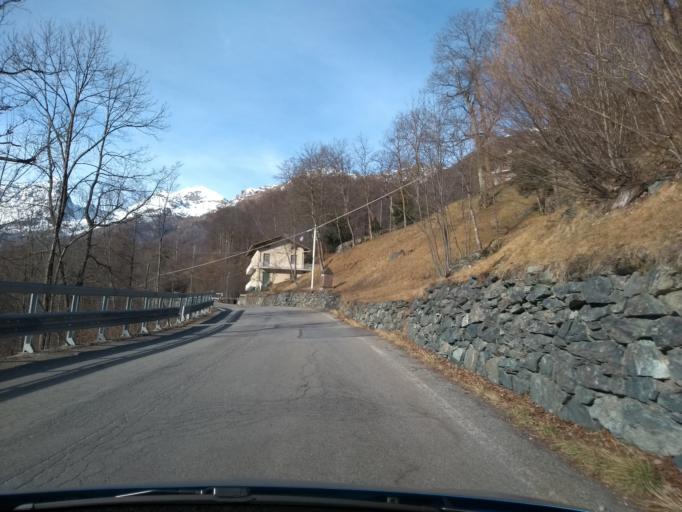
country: IT
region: Piedmont
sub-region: Provincia di Torino
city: Ala di Stura
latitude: 45.3114
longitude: 7.3211
